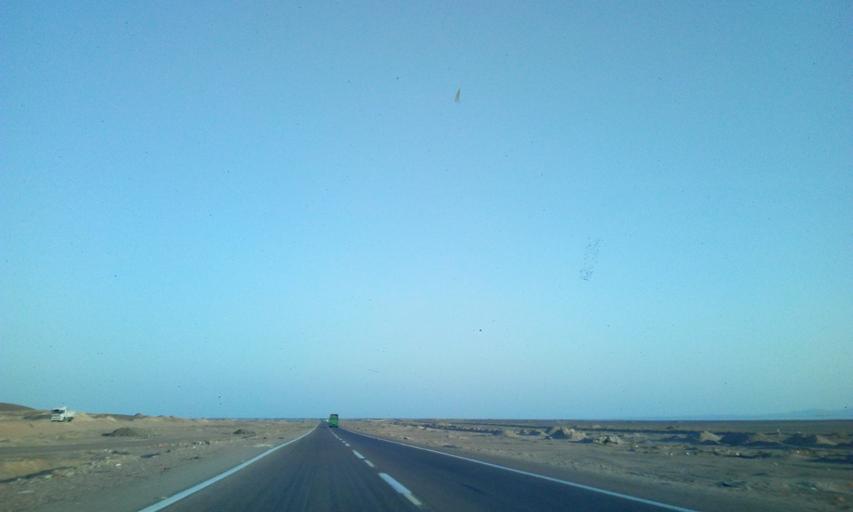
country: EG
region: South Sinai
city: Tor
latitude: 28.0184
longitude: 33.3073
